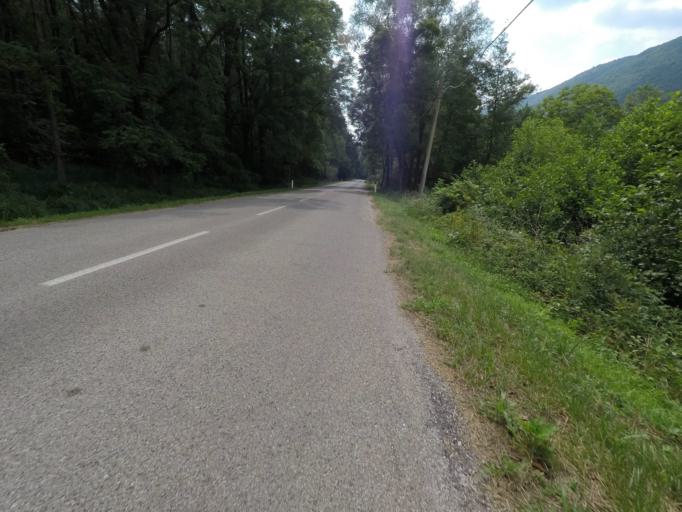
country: IT
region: Friuli Venezia Giulia
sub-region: Provincia di Pordenone
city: Polcenigo
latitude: 46.0226
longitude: 12.4868
